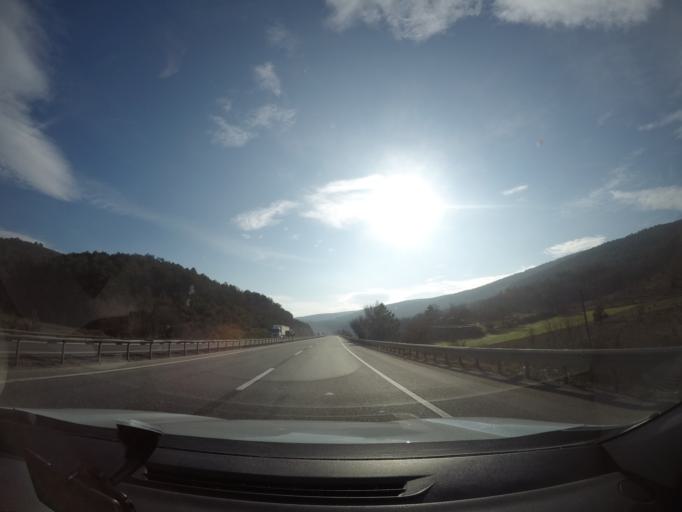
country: TR
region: Bilecik
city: Dodurga
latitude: 39.8895
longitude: 29.9245
